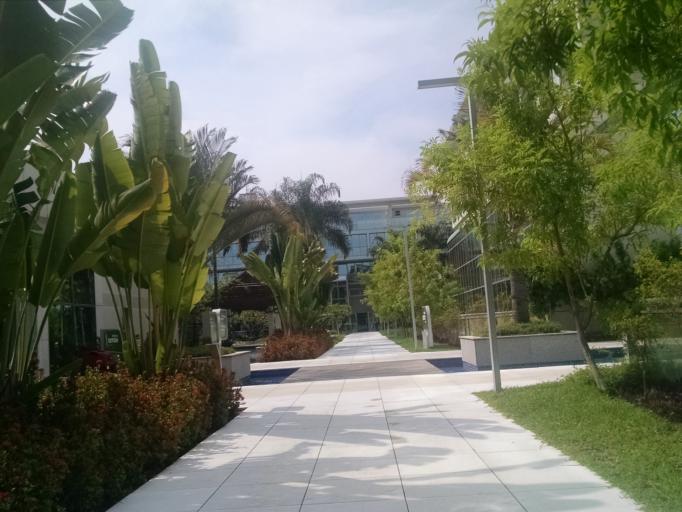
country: BR
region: Rio de Janeiro
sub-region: Rio De Janeiro
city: Rio de Janeiro
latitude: -22.9892
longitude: -43.3591
